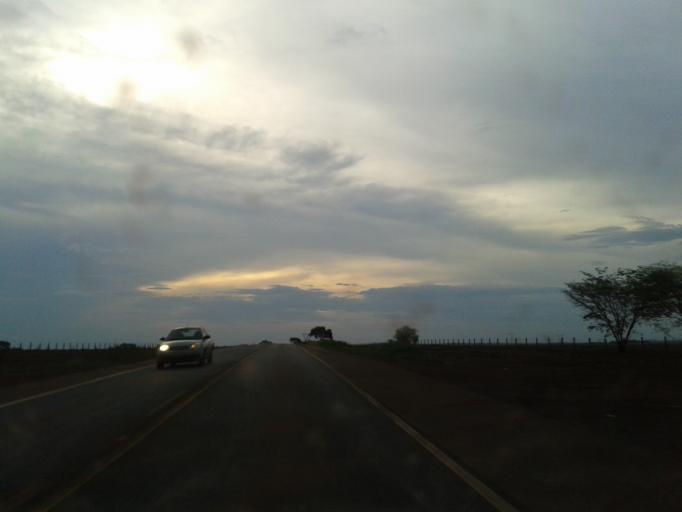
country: BR
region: Goias
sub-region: Santa Helena De Goias
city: Santa Helena de Goias
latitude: -17.8903
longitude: -50.6674
